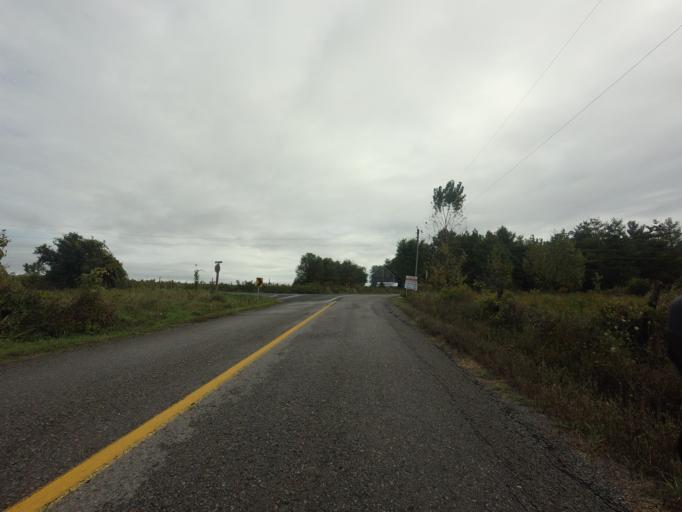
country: CA
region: Ontario
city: Oshawa
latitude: 43.9032
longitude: -78.5204
